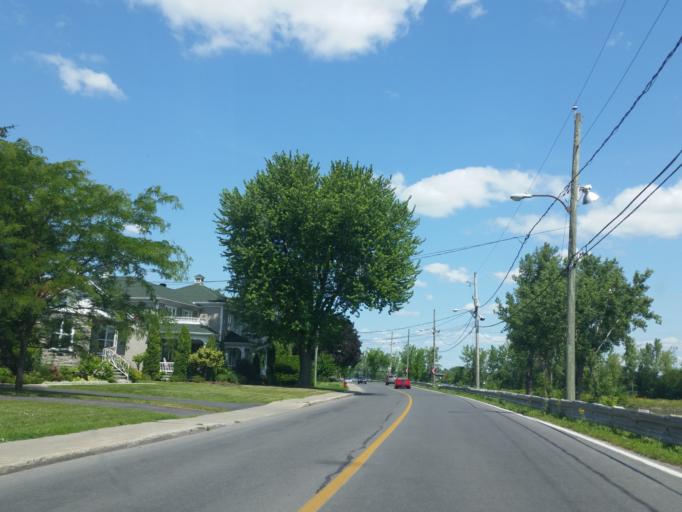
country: CA
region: Quebec
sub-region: Monteregie
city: Saint-Jean-sur-Richelieu
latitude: 45.3161
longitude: -73.2530
